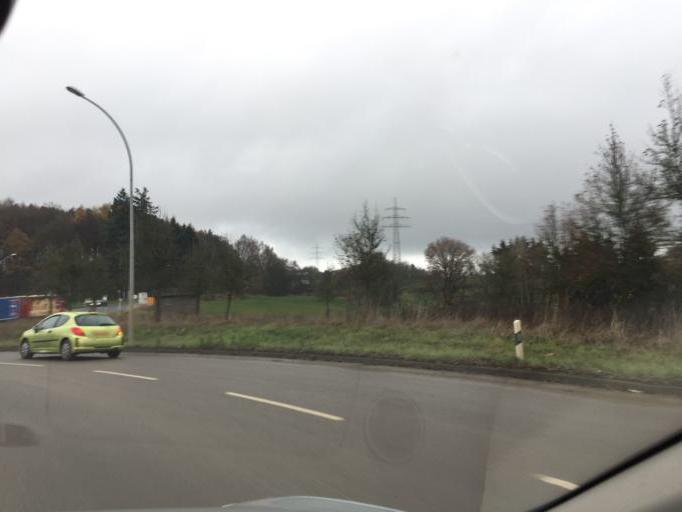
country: LU
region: Diekirch
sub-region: Canton de Diekirch
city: Diekirch
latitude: 49.8861
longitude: 6.1373
